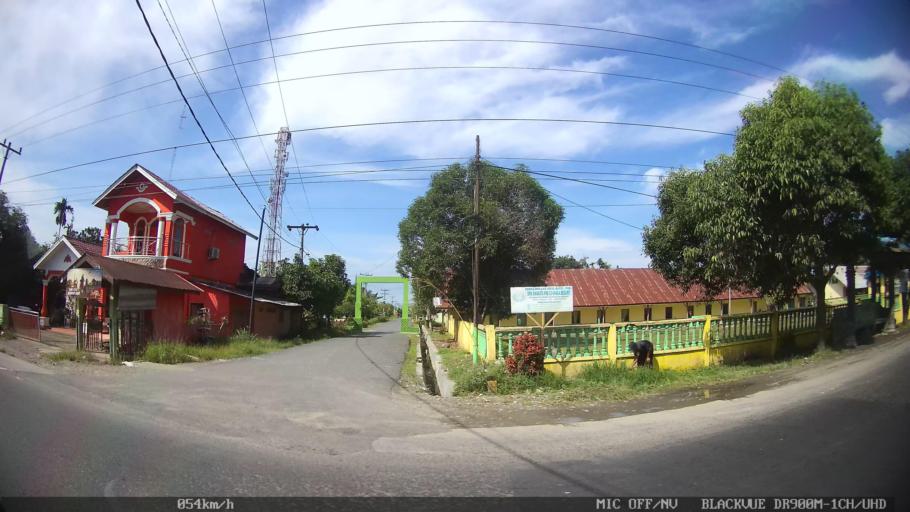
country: ID
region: North Sumatra
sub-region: Kabupaten Langkat
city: Stabat
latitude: 3.7276
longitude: 98.4965
